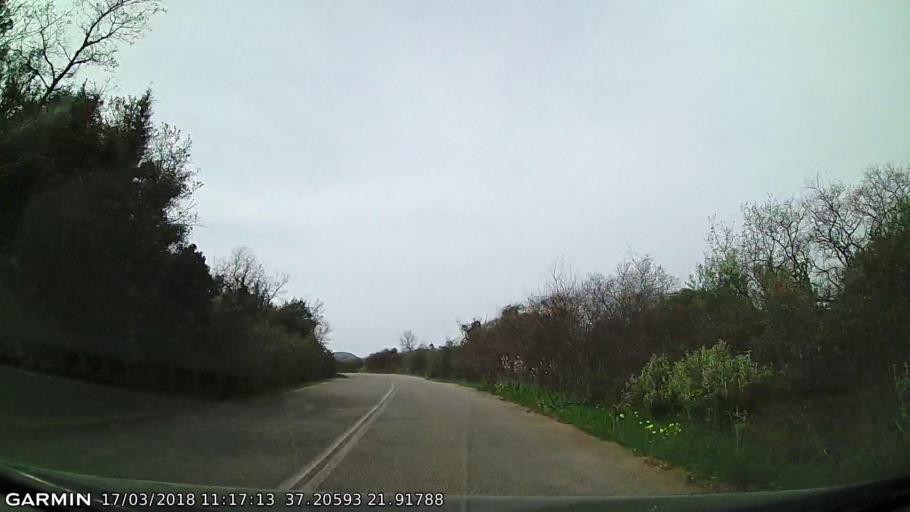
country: GR
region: Peloponnese
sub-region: Nomos Messinias
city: Meligalas
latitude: 37.2059
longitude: 21.9177
